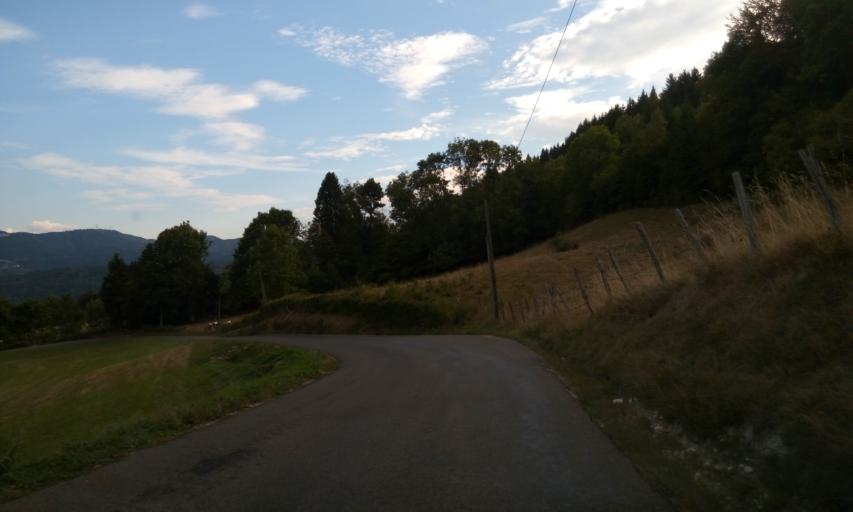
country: FR
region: Rhone-Alpes
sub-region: Departement de l'Ain
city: Martignat
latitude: 46.1868
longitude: 5.6780
